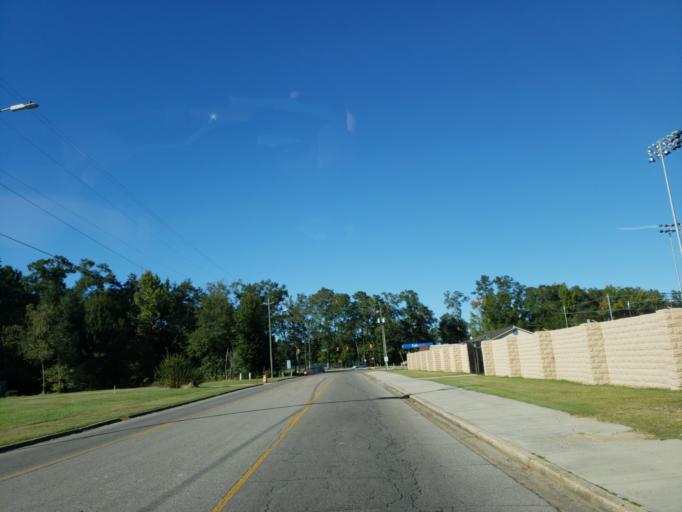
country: US
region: Mississippi
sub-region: Forrest County
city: Hattiesburg
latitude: 31.3305
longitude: -89.3100
